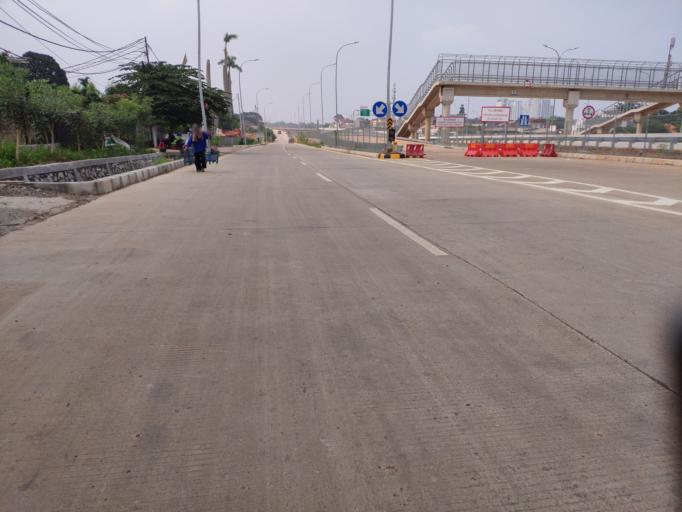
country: ID
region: West Java
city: Pamulang
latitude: -6.3272
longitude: 106.8015
